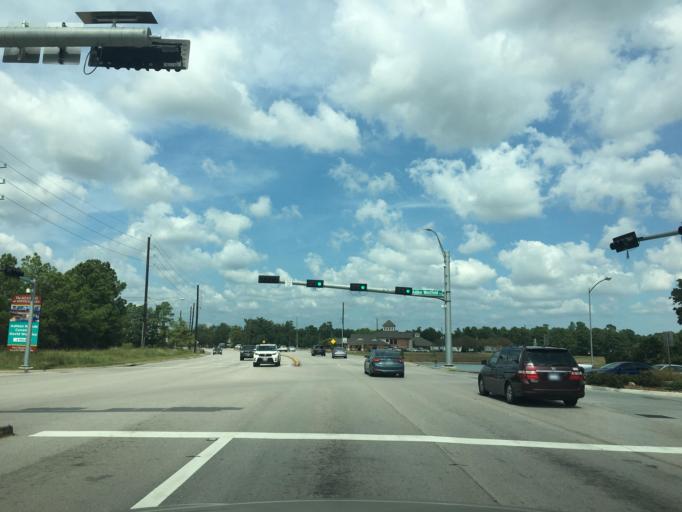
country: US
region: Texas
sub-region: Harris County
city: Spring
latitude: 30.1222
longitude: -95.4015
